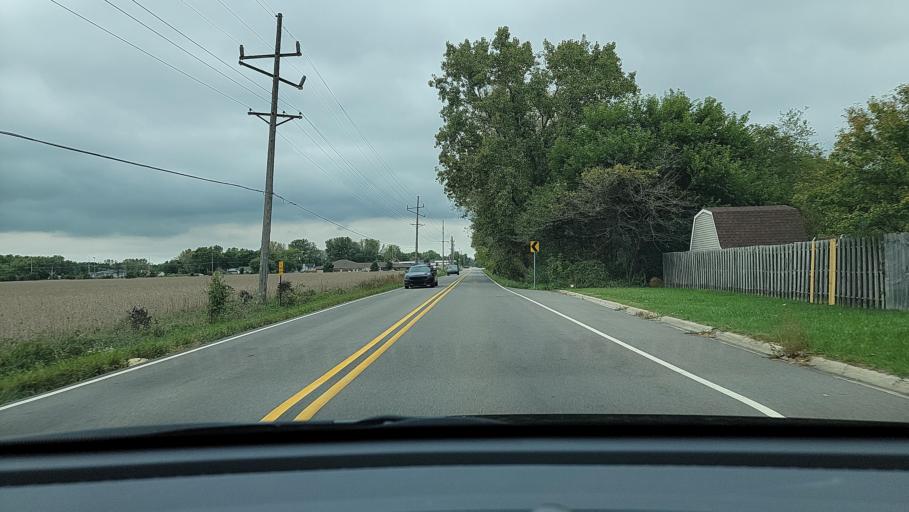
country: US
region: Indiana
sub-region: Porter County
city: Portage
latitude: 41.5466
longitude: -87.1971
